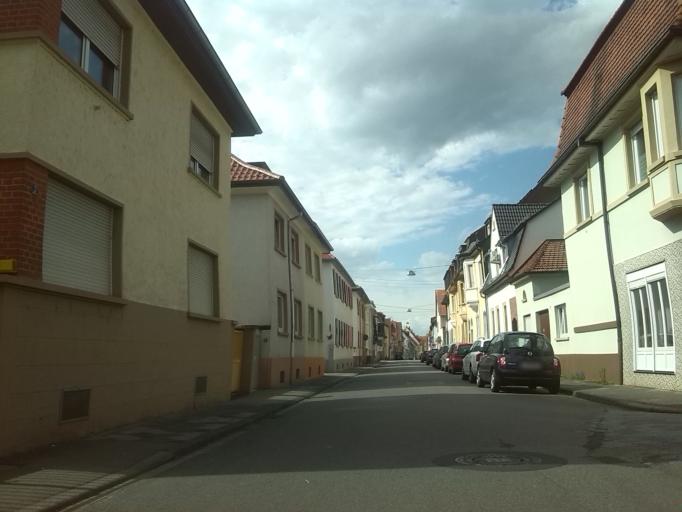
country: DE
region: Baden-Wuerttemberg
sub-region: Karlsruhe Region
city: Ilvesheim
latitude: 49.4614
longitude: 8.5617
